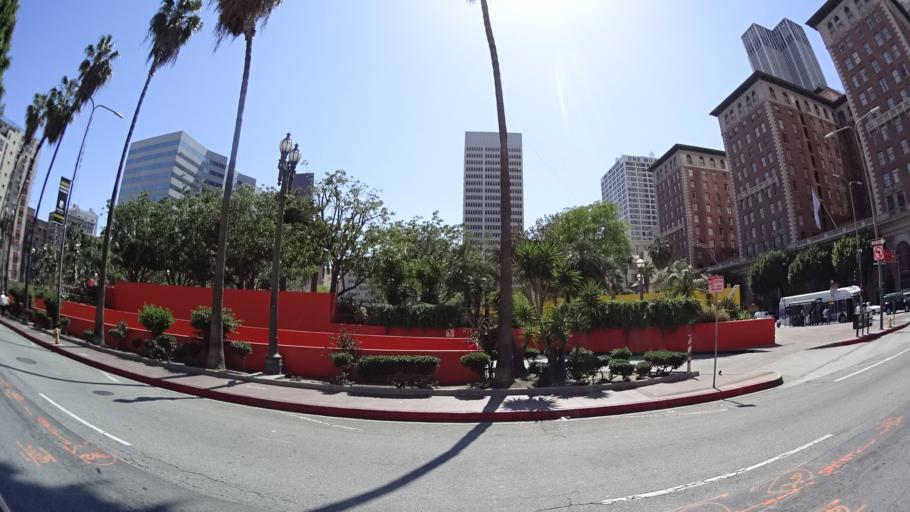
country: US
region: California
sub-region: Los Angeles County
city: Los Angeles
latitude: 34.0492
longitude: -118.2524
